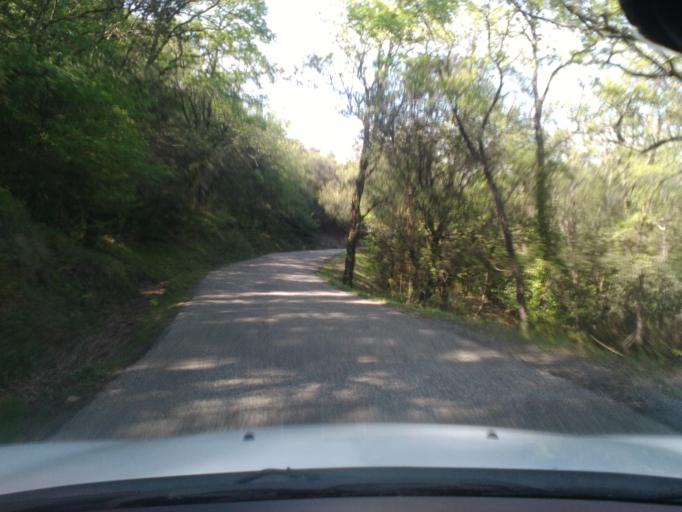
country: FR
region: Languedoc-Roussillon
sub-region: Departement du Gard
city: Lasalle
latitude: 44.0151
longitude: 3.8736
